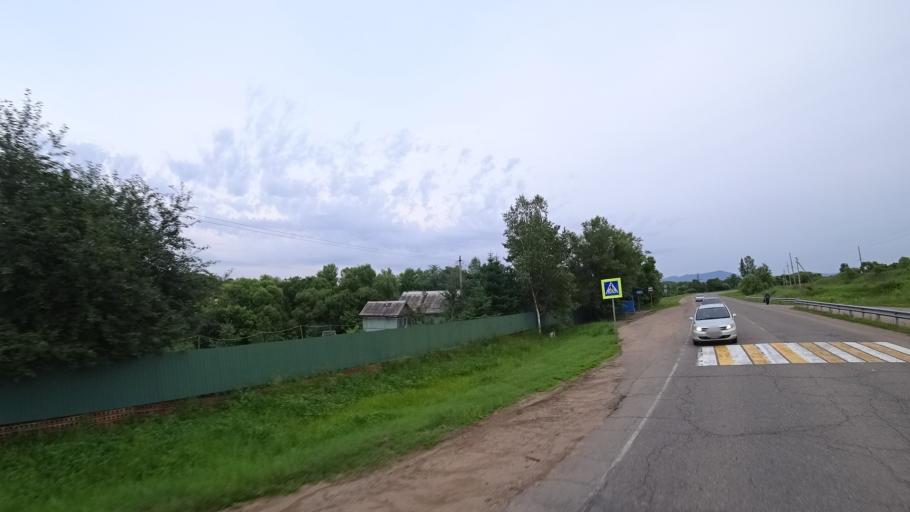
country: RU
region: Primorskiy
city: Novosysoyevka
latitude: 44.2266
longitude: 133.3509
